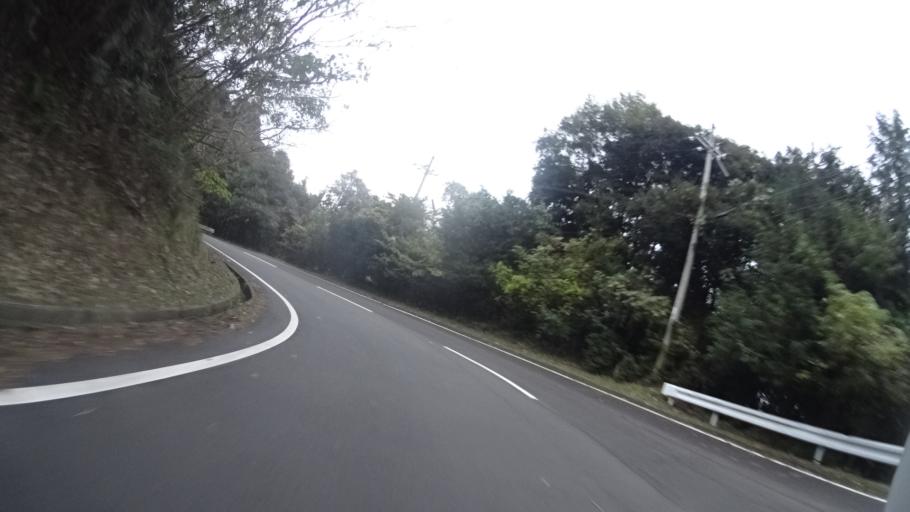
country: JP
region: Kyoto
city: Maizuru
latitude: 35.5681
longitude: 135.4511
